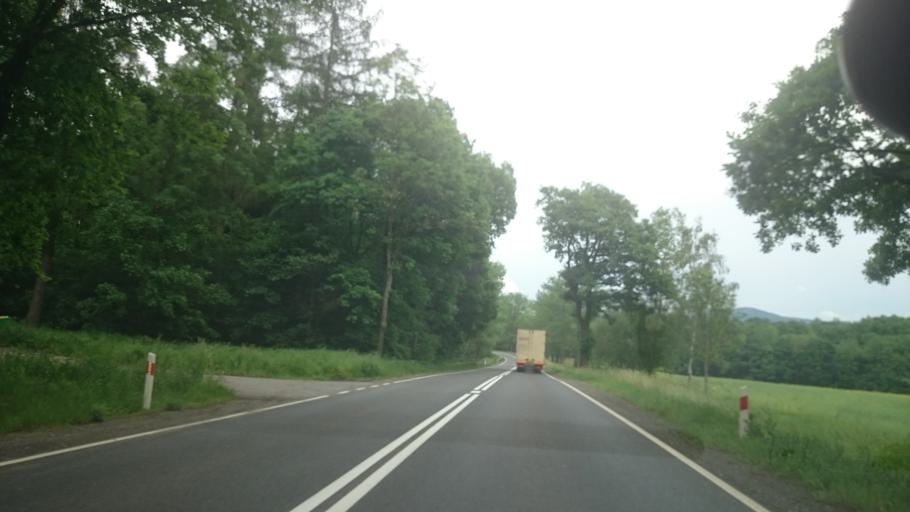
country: PL
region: Lower Silesian Voivodeship
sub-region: Powiat klodzki
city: Klodzko
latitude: 50.4300
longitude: 16.7235
